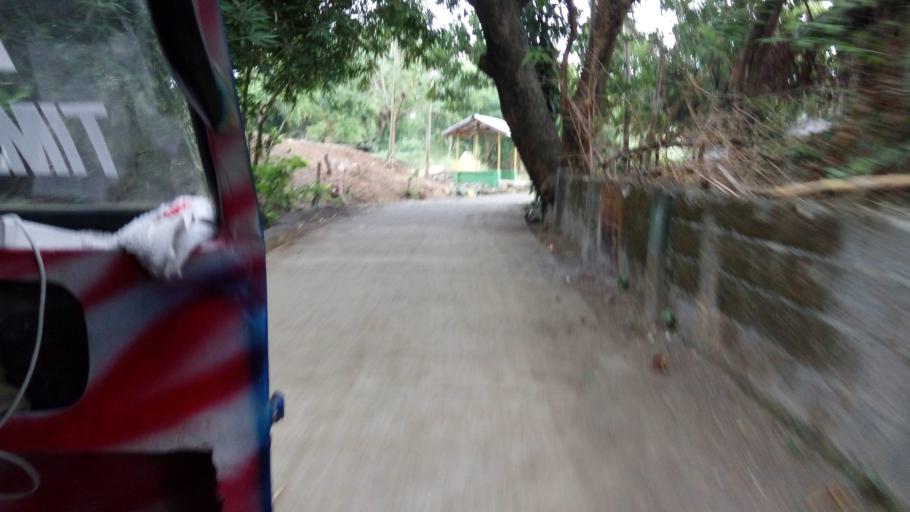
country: PH
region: Ilocos
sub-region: Province of La Union
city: Santo Tomas
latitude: 16.2883
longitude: 120.3807
